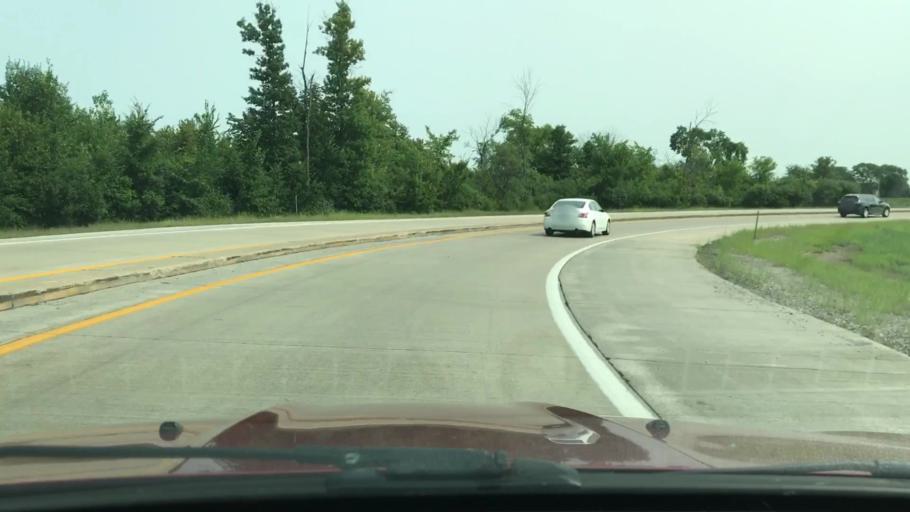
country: US
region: Ohio
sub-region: Wood County
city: Millbury
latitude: 41.5251
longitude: -83.4574
